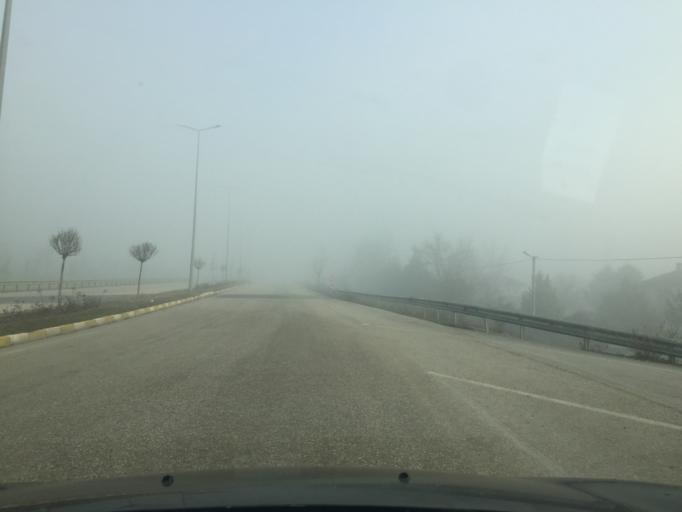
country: TR
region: Duzce
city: Duzce
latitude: 40.8654
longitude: 31.2168
